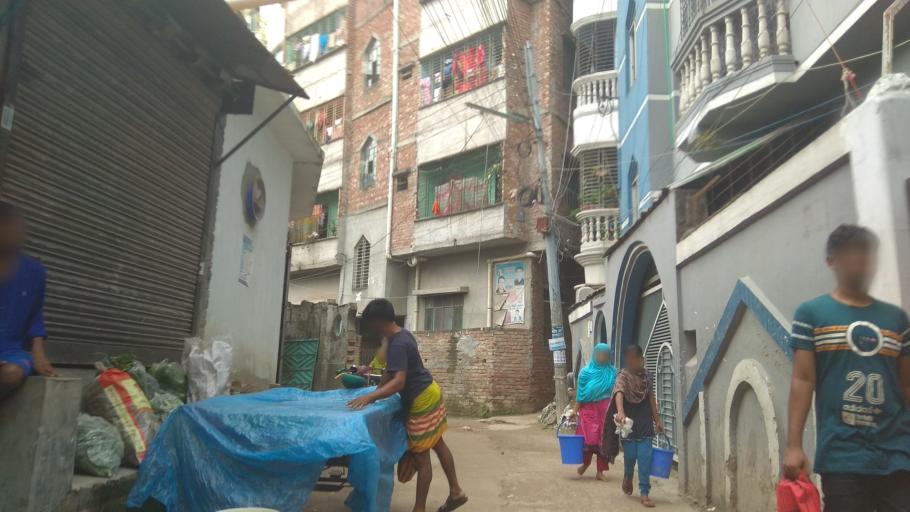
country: BD
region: Dhaka
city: Azimpur
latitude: 23.8026
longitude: 90.3732
